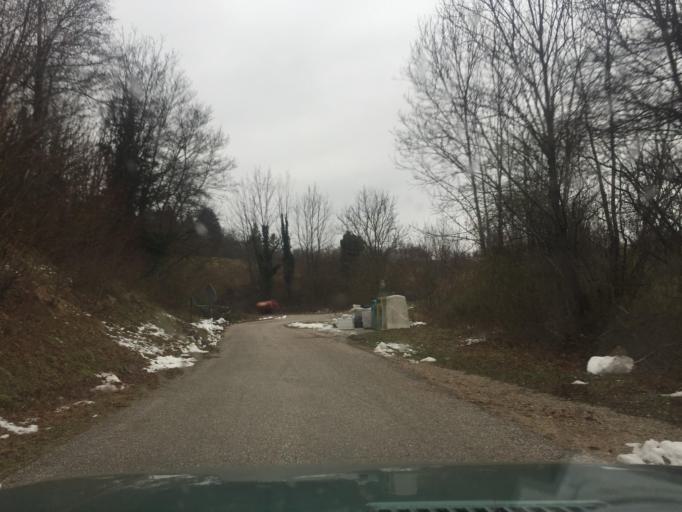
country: SI
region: Kanal
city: Kanal
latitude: 46.0744
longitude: 13.6645
